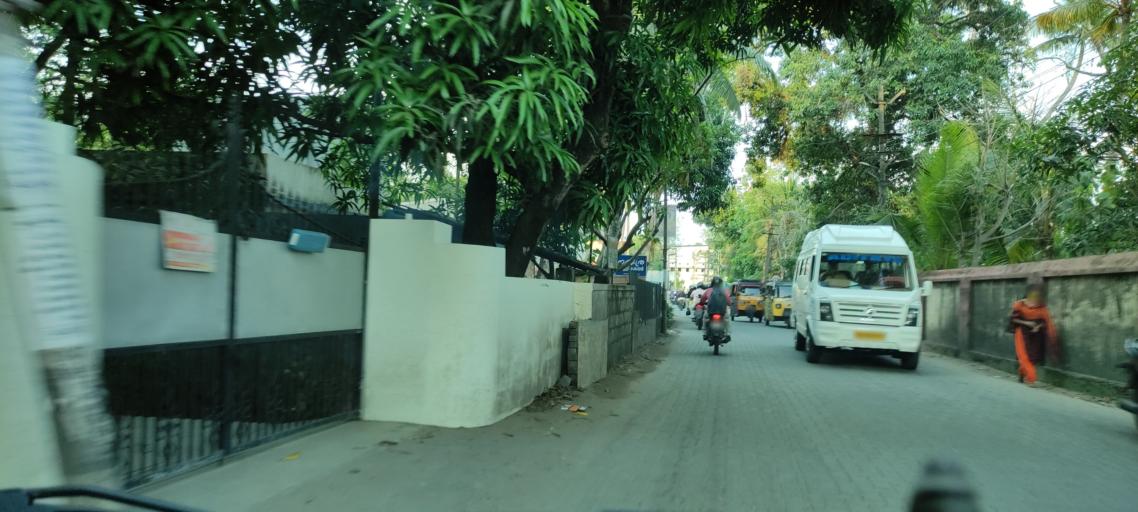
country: IN
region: Kerala
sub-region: Alappuzha
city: Arukutti
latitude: 9.8678
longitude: 76.3060
